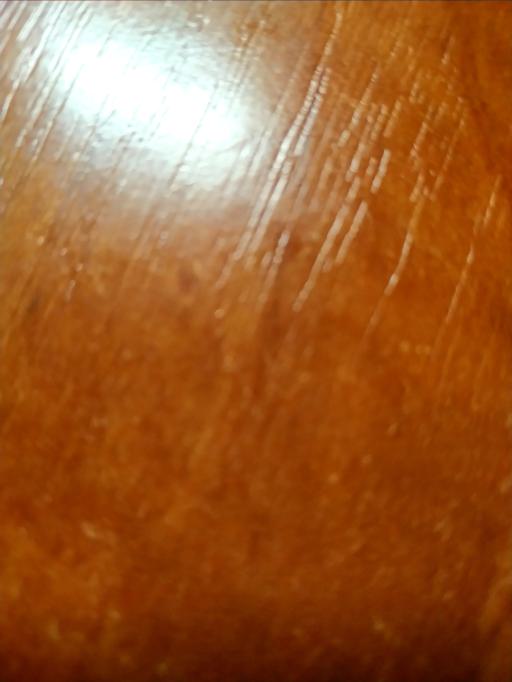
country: RU
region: Kaluga
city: Iznoski
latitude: 54.8769
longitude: 35.4430
